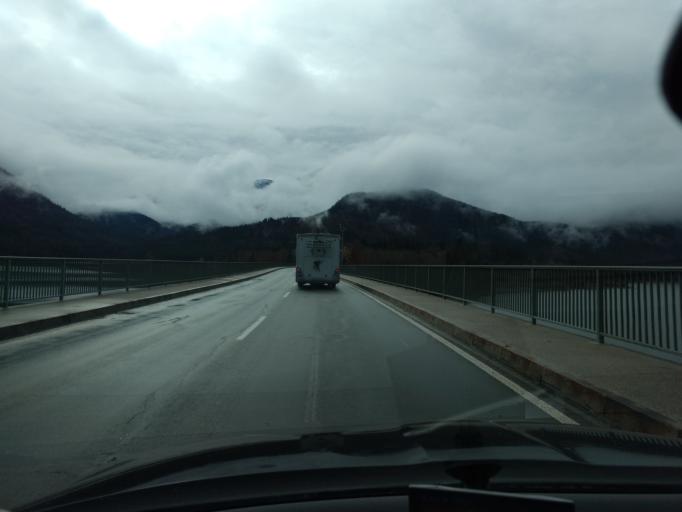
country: DE
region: Bavaria
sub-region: Upper Bavaria
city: Jachenau
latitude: 47.5770
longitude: 11.5374
